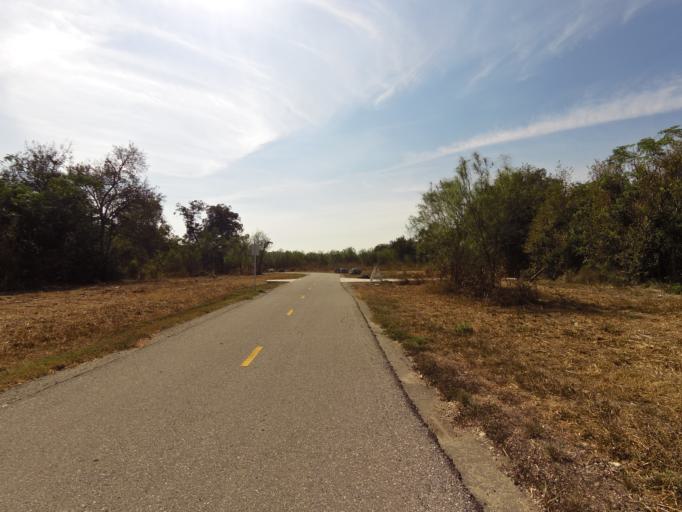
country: US
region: Texas
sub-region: Bexar County
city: Kirby
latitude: 29.4397
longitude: -98.4209
